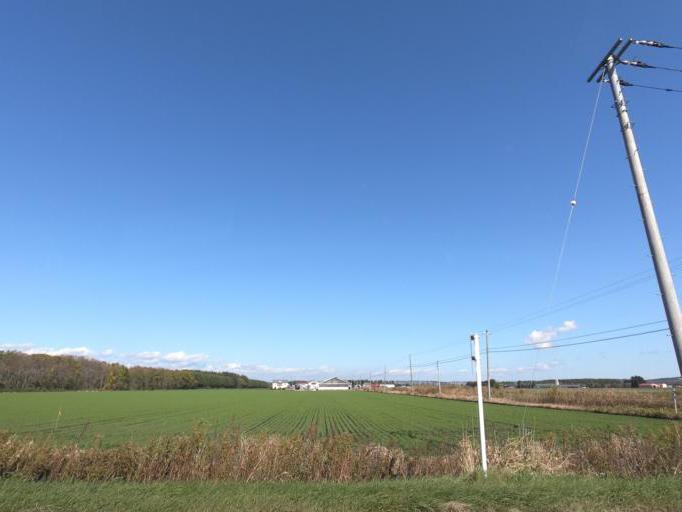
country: JP
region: Hokkaido
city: Otofuke
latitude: 43.0610
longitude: 143.2630
